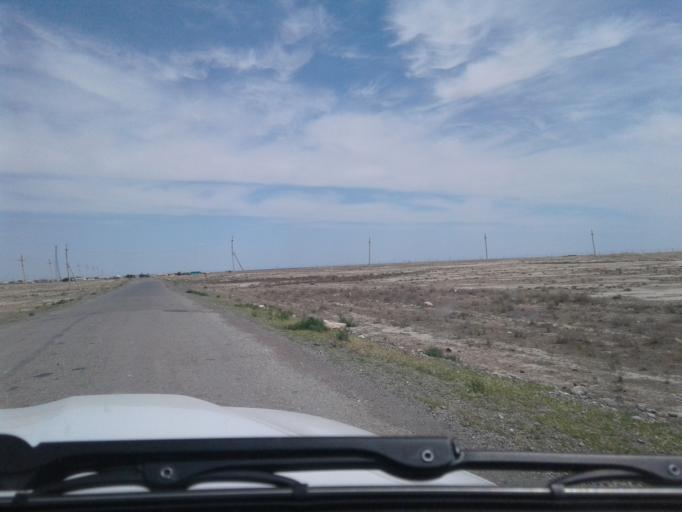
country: TM
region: Balkan
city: Gazanjyk
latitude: 39.2002
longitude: 55.7083
